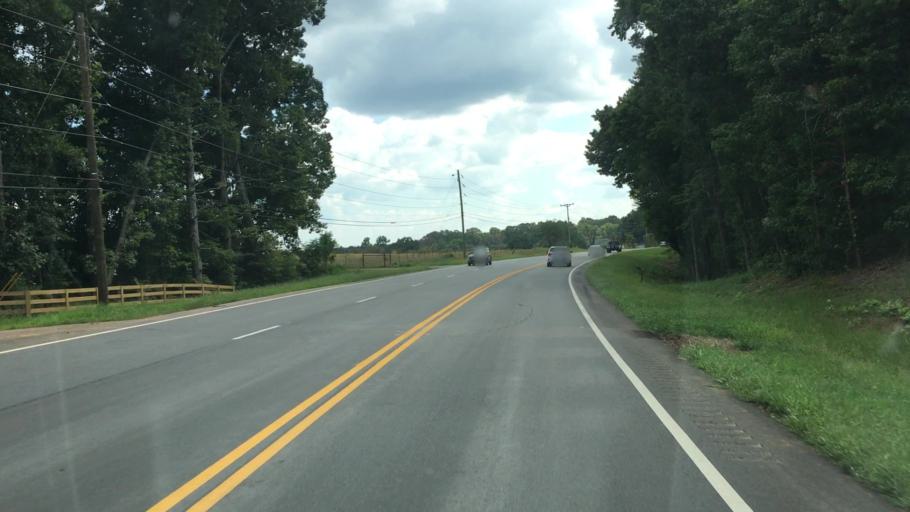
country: US
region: Georgia
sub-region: Putnam County
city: Jefferson
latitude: 33.4243
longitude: -83.3701
